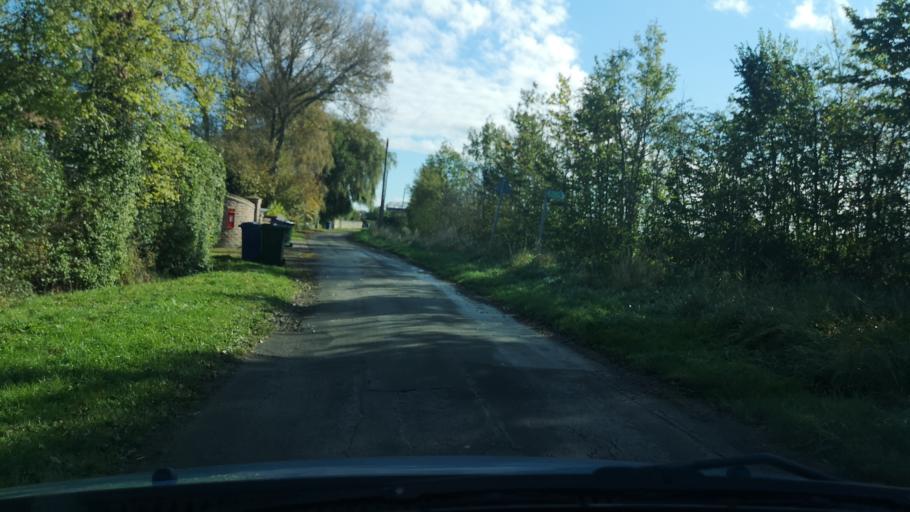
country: GB
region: England
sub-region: Doncaster
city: Fenwick
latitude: 53.6369
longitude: -1.1067
